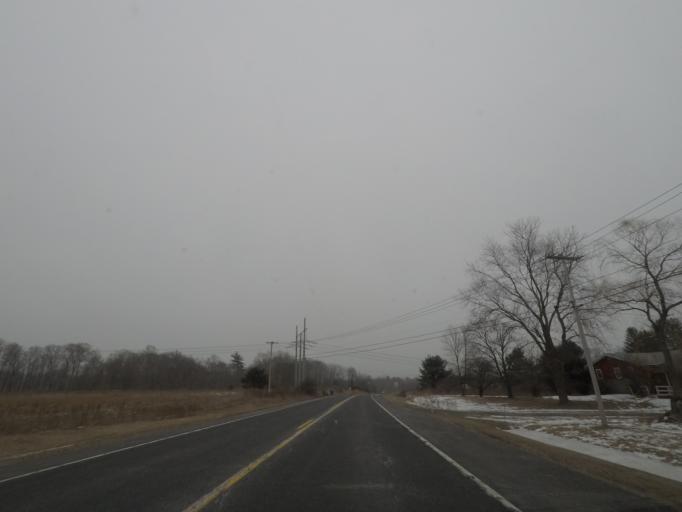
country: US
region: New York
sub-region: Albany County
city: Delmar
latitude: 42.5603
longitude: -73.8152
